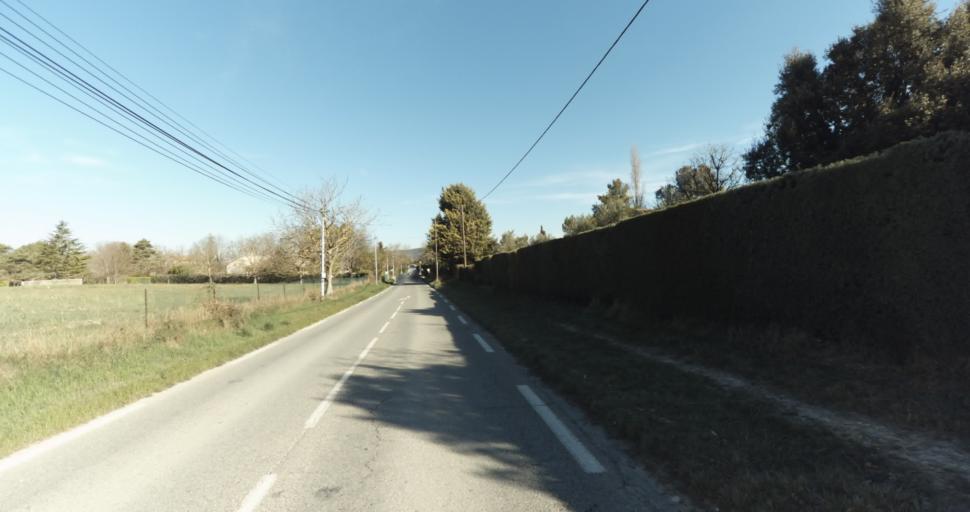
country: FR
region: Provence-Alpes-Cote d'Azur
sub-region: Departement des Bouches-du-Rhone
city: Aix-en-Provence
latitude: 43.5700
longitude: 5.4248
